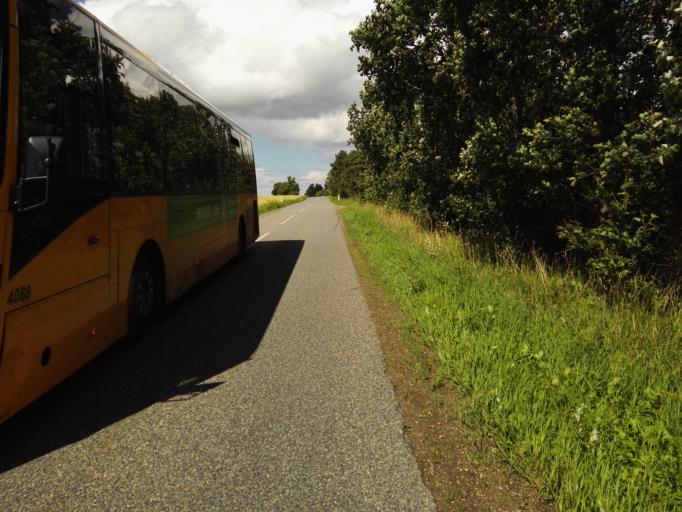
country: DK
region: Capital Region
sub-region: Egedal Kommune
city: Vekso
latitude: 55.7815
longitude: 12.2336
